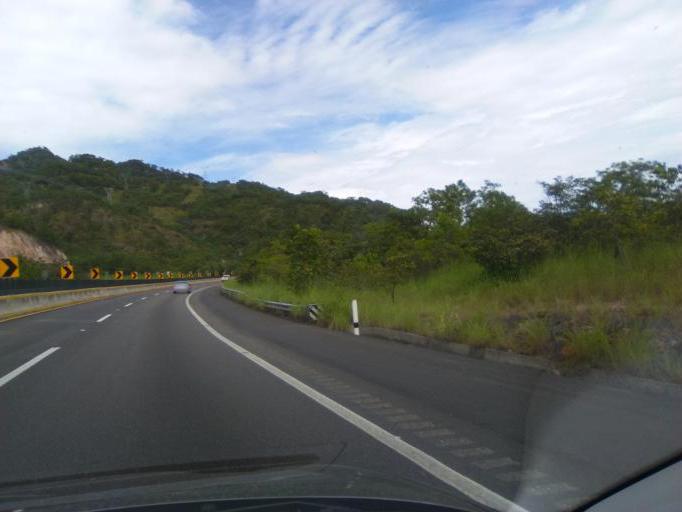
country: MX
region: Guerrero
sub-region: Chilpancingo de los Bravo
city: Cajelitos
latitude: 17.2984
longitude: -99.5033
